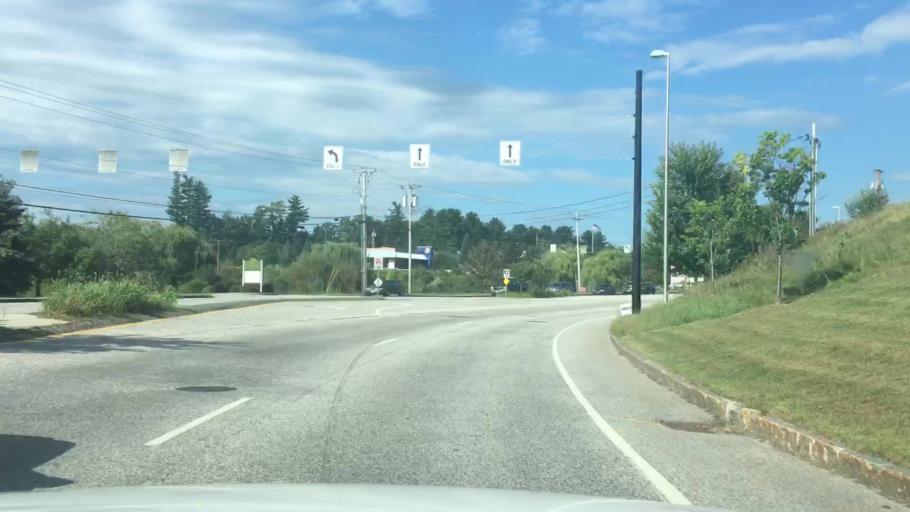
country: US
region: Maine
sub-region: Androscoggin County
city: Auburn
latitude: 44.1204
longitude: -70.2340
